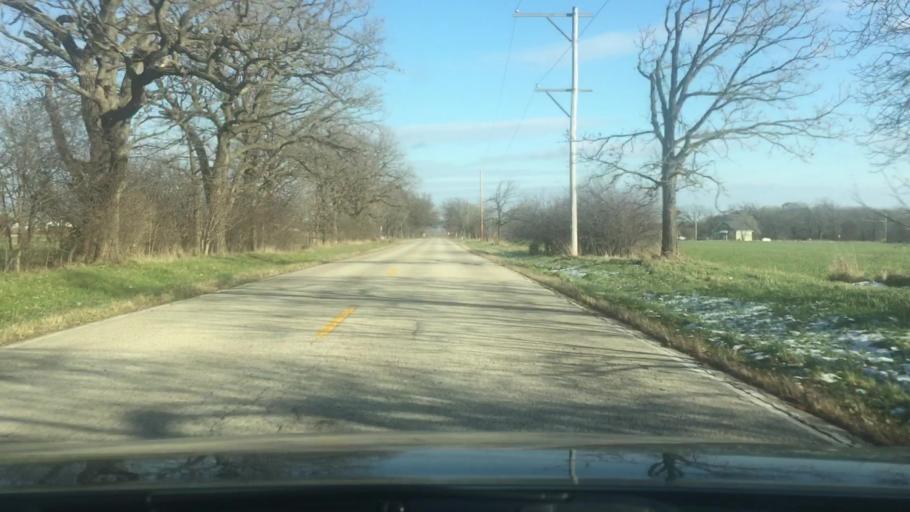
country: US
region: Wisconsin
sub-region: Waukesha County
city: Eagle
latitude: 42.9172
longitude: -88.5271
